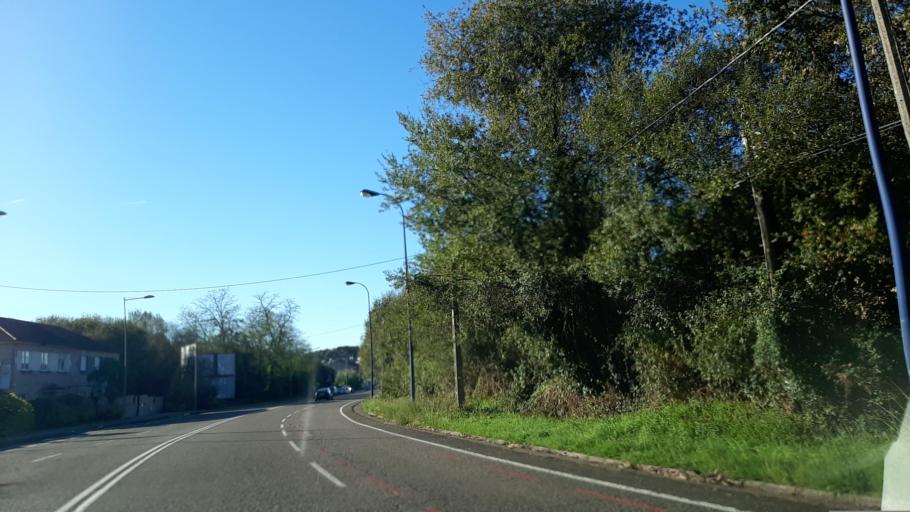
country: ES
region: Galicia
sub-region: Provincia de Pontevedra
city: Vigo
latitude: 42.2110
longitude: -8.7697
